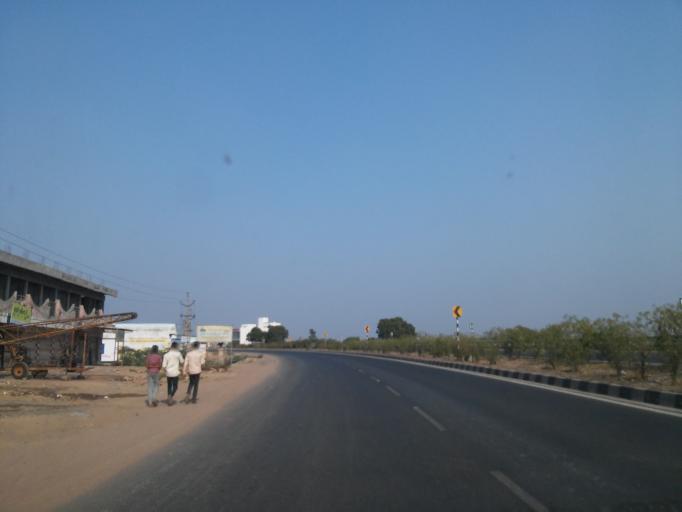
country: IN
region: Gujarat
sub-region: Surendranagar
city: Halvad
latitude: 23.0040
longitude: 71.1906
